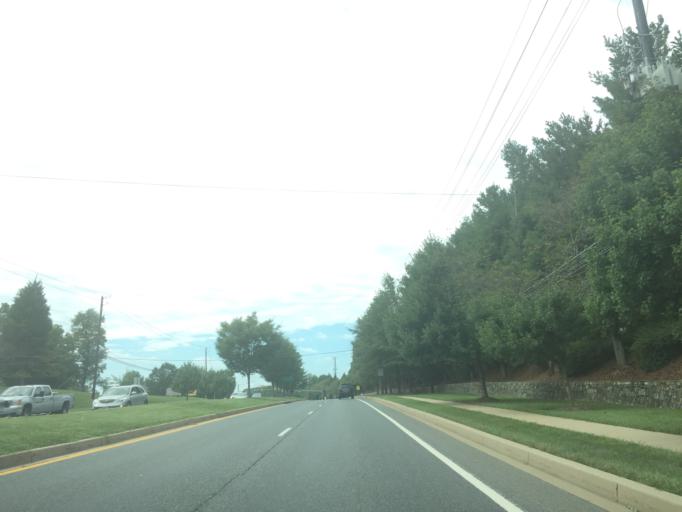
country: US
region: Maryland
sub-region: Montgomery County
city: North Potomac
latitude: 39.1145
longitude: -77.2439
